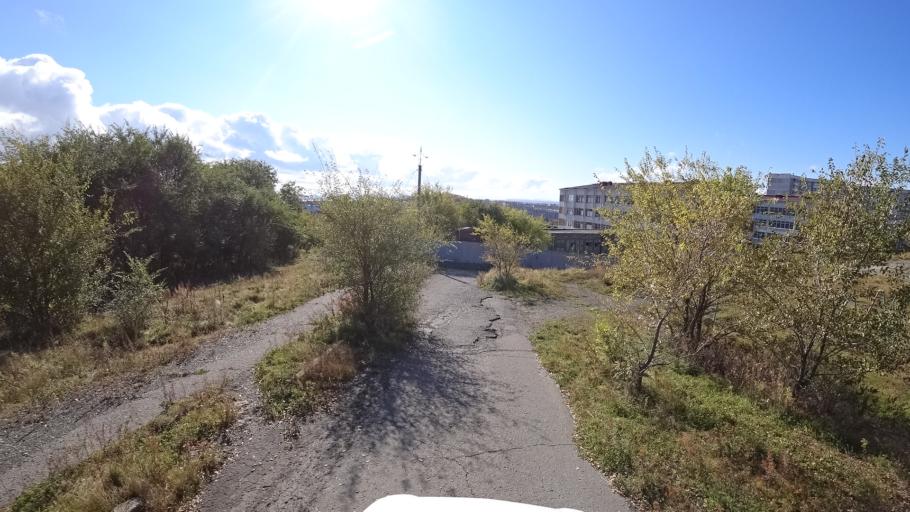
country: RU
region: Khabarovsk Krai
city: Amursk
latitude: 50.2389
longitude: 136.9178
